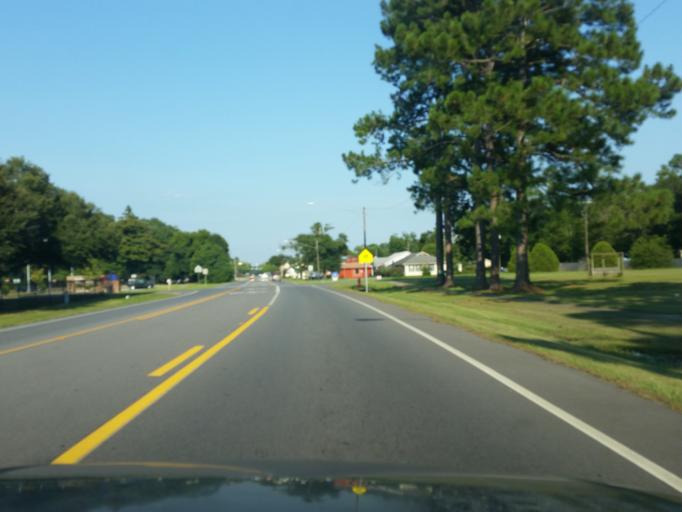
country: US
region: Alabama
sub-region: Baldwin County
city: Foley
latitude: 30.4064
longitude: -87.6903
